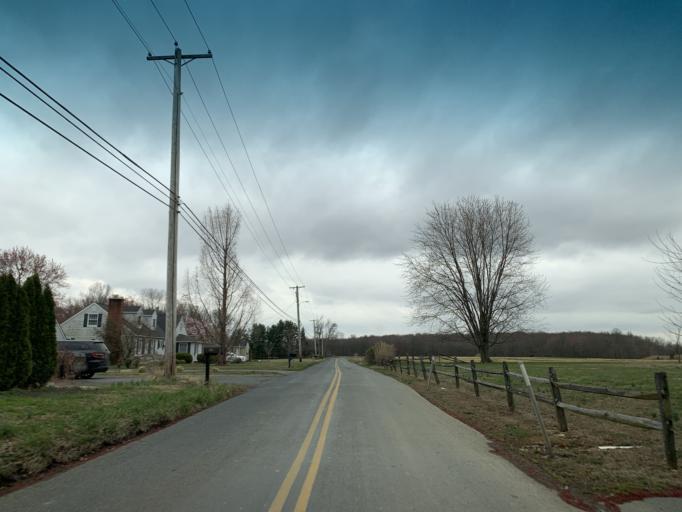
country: US
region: Maryland
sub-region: Harford County
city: Aberdeen
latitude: 39.5630
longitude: -76.1958
